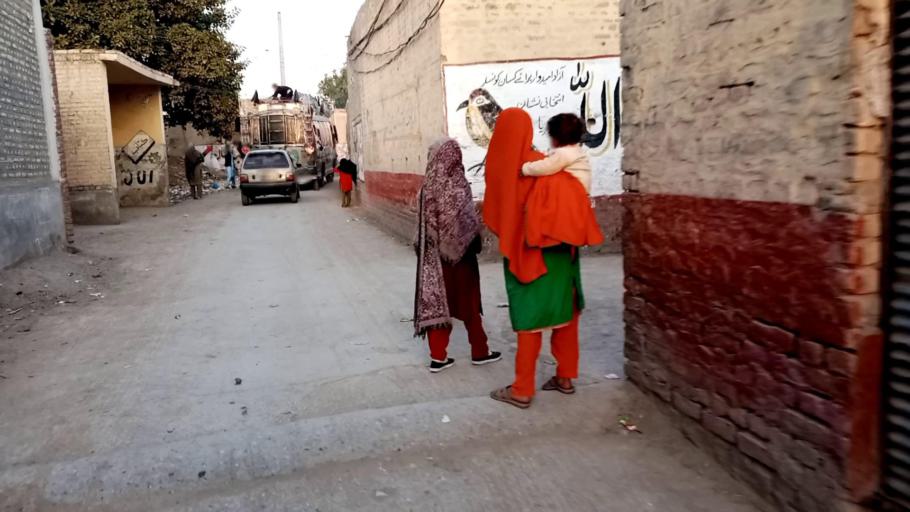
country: PK
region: Khyber Pakhtunkhwa
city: Peshawar
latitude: 34.0516
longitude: 71.4618
